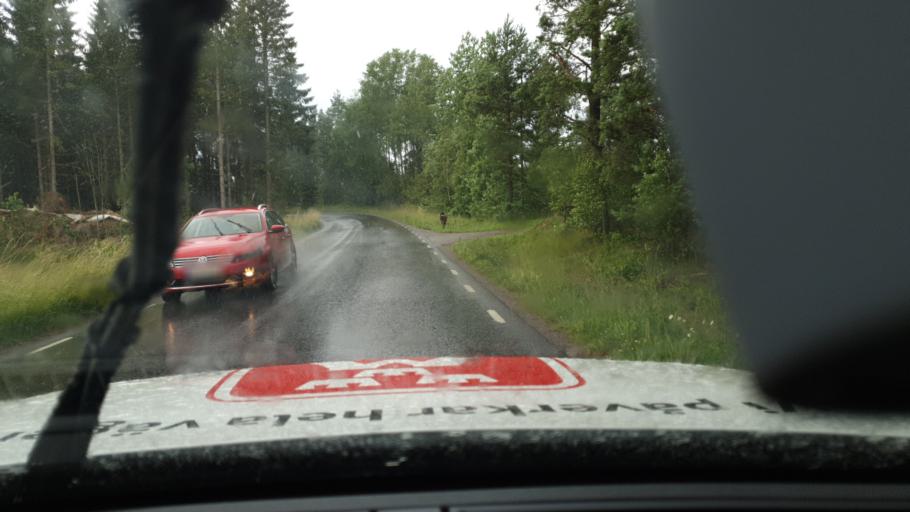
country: SE
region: Vaestra Goetaland
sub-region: Falkopings Kommun
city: Akarp
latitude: 58.2438
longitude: 13.6019
